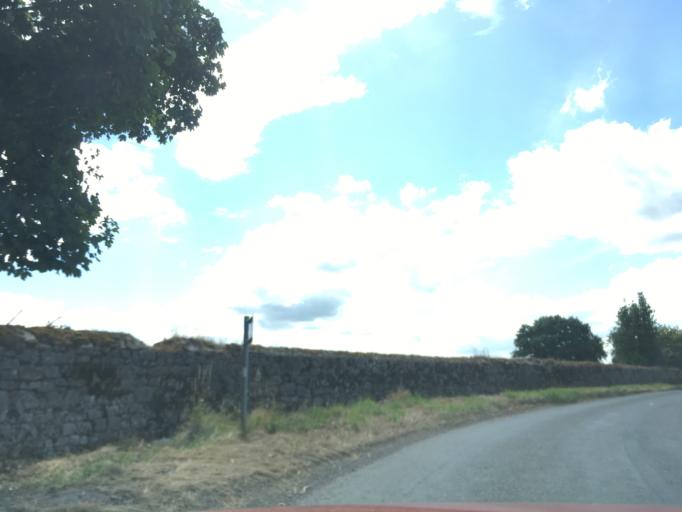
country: IE
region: Munster
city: Cahir
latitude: 52.3515
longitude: -7.9347
